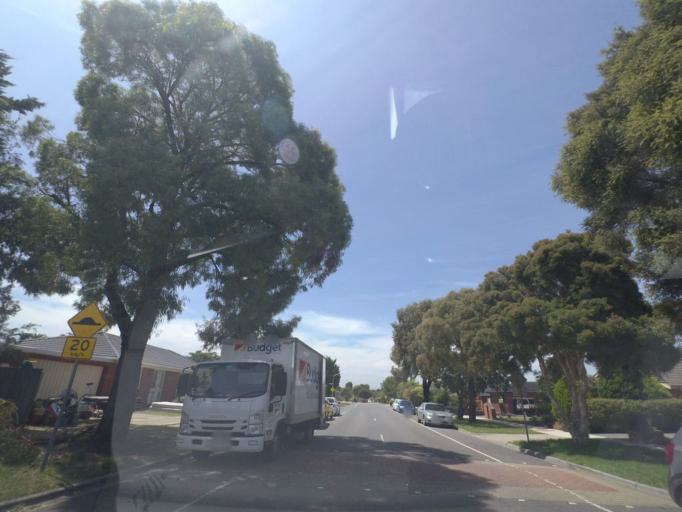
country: AU
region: Victoria
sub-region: Brimbank
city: Taylors Lakes
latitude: -37.7110
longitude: 144.7895
